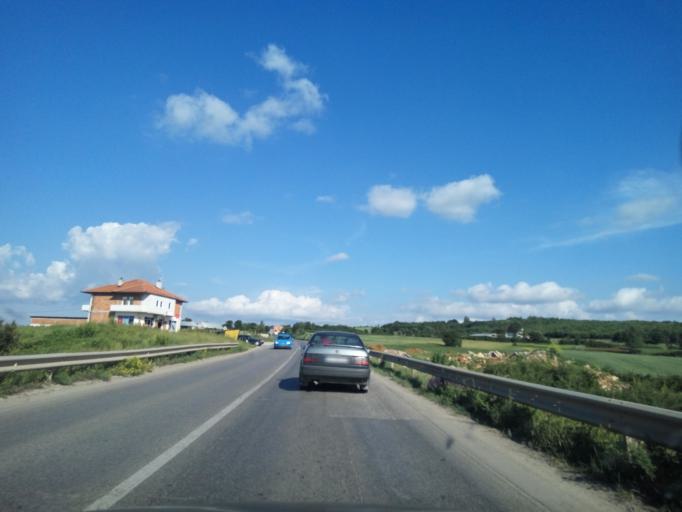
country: XK
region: Pec
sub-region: Komuna e Klines
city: Klina
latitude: 42.5886
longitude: 20.6696
